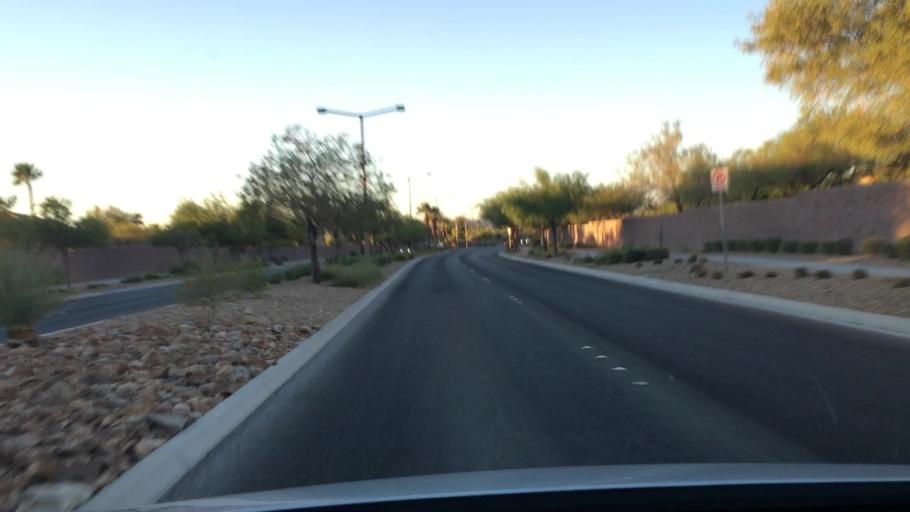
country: US
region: Nevada
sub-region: Clark County
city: Summerlin South
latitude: 36.1369
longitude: -115.3424
